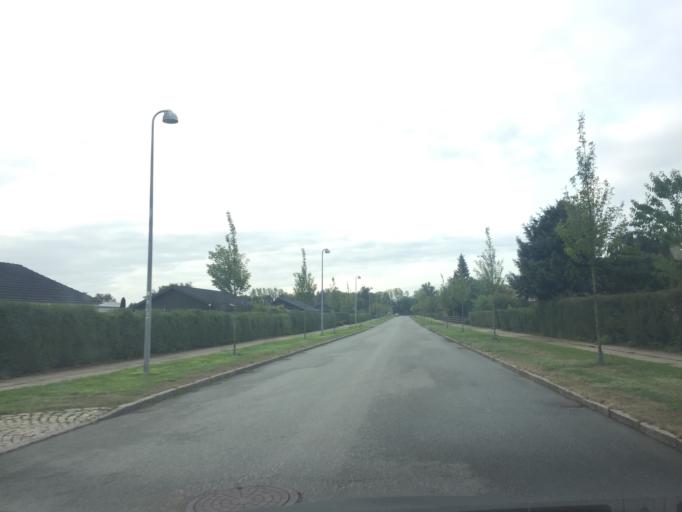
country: DK
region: Capital Region
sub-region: Albertslund Kommune
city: Albertslund
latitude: 55.6465
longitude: 12.3632
